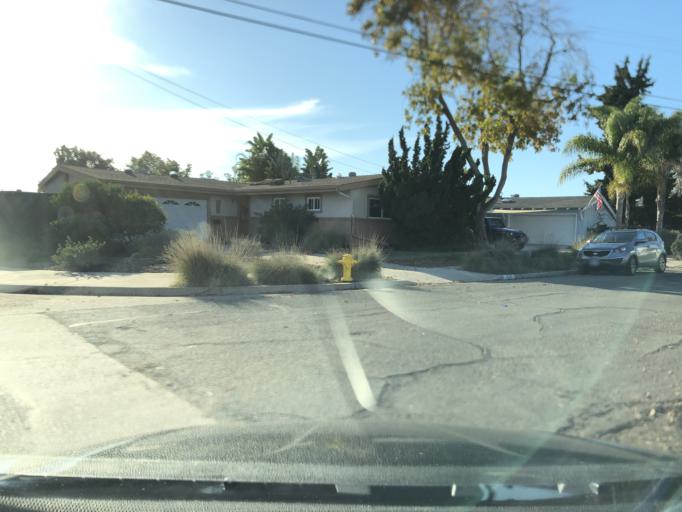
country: US
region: California
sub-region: San Diego County
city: La Jolla
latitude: 32.8254
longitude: -117.1947
